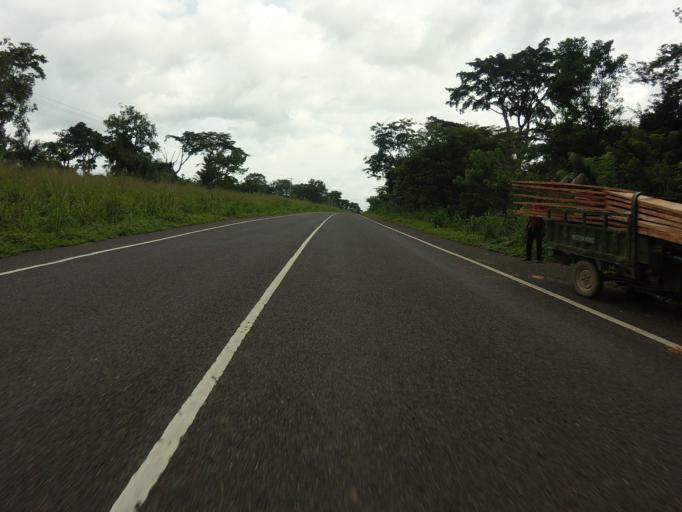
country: TG
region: Plateaux
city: Badou
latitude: 7.9813
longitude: 0.5606
